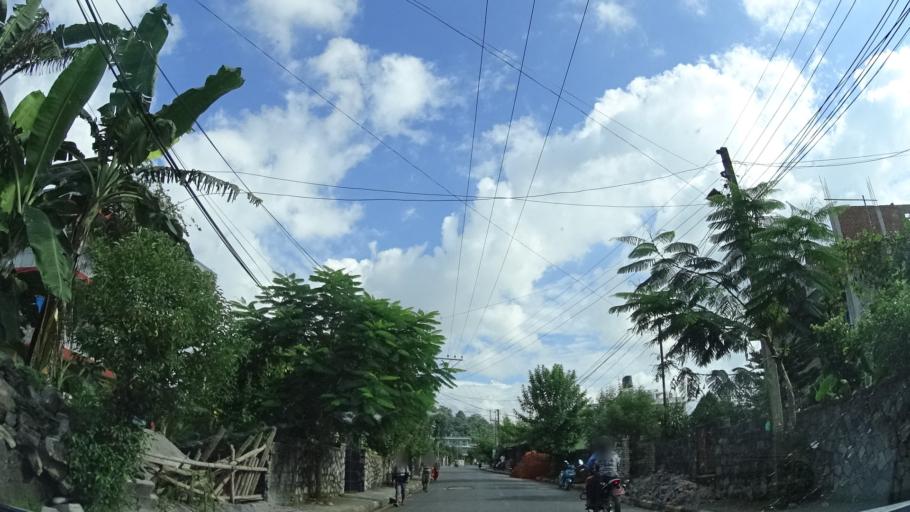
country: NP
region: Western Region
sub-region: Gandaki Zone
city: Pokhara
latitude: 28.2087
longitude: 83.9645
